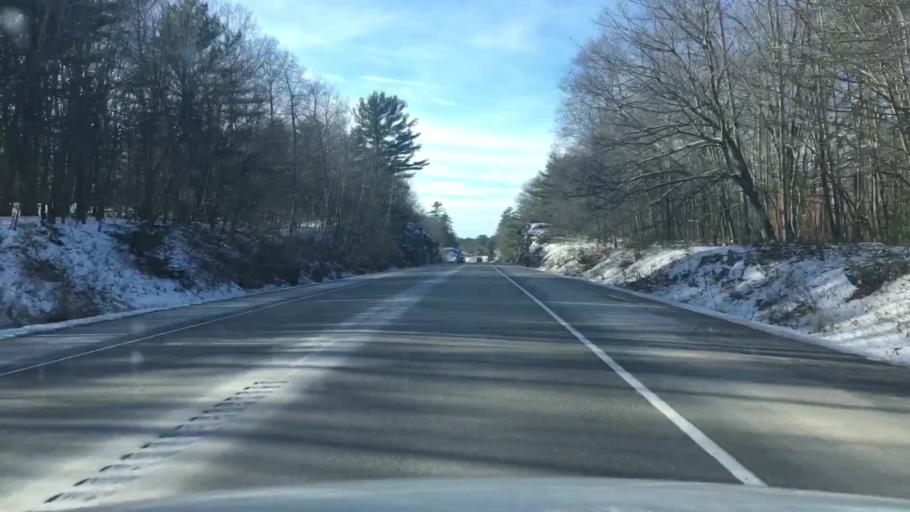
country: US
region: Maine
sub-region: Sagadahoc County
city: Woolwich
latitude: 43.9385
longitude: -69.7698
